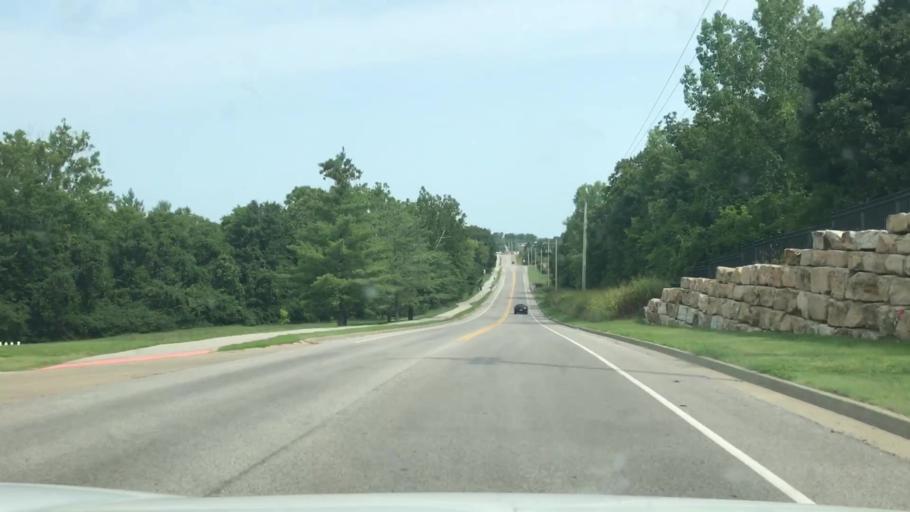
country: US
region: Missouri
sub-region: Saint Charles County
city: Cottleville
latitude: 38.7194
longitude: -90.6421
